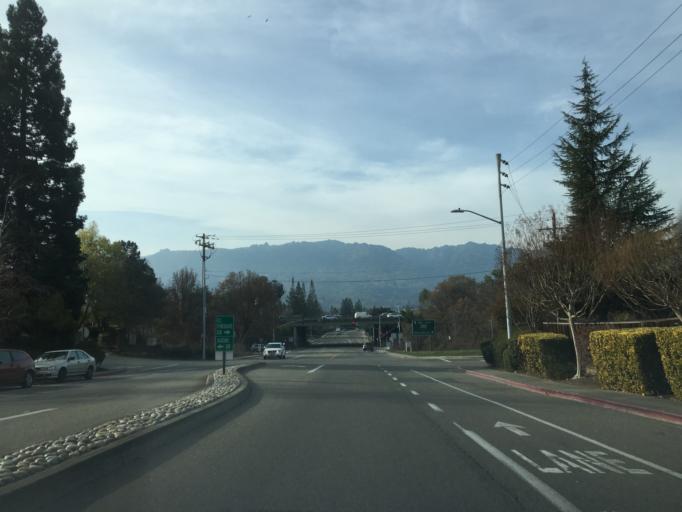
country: US
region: California
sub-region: Contra Costa County
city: Danville
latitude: 37.8309
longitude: -121.9990
